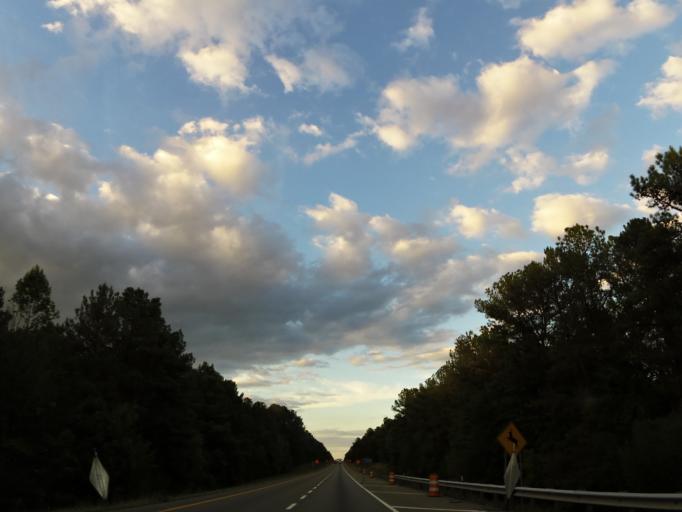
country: US
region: Tennessee
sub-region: Bradley County
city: Hopewell
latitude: 35.2592
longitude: -84.8329
